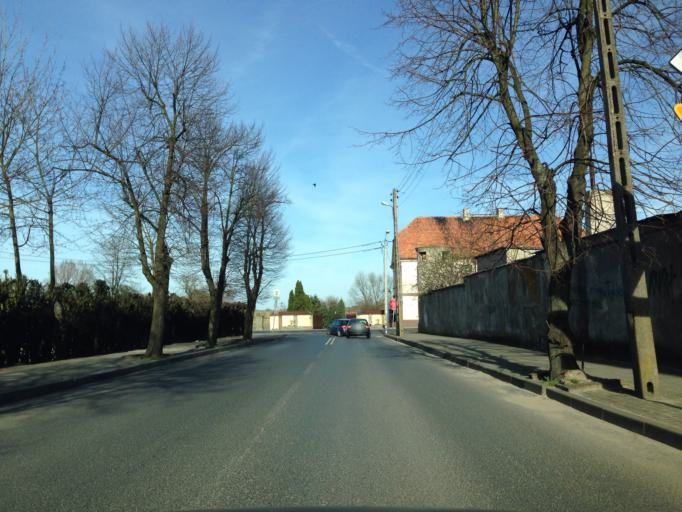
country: PL
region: Lodz Voivodeship
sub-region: Powiat leczycki
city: Leczyca
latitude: 52.0615
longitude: 19.2021
